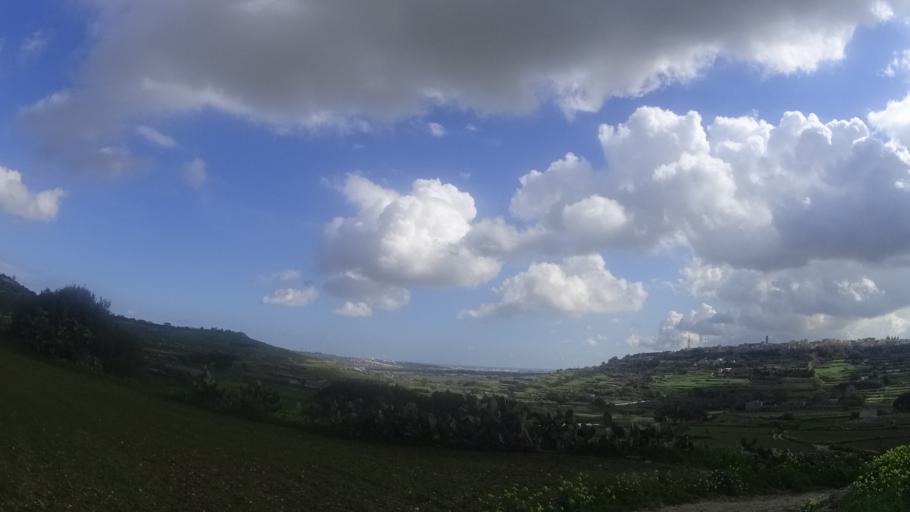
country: MT
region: L-Imtarfa
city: Imtarfa
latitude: 35.8986
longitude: 14.3873
